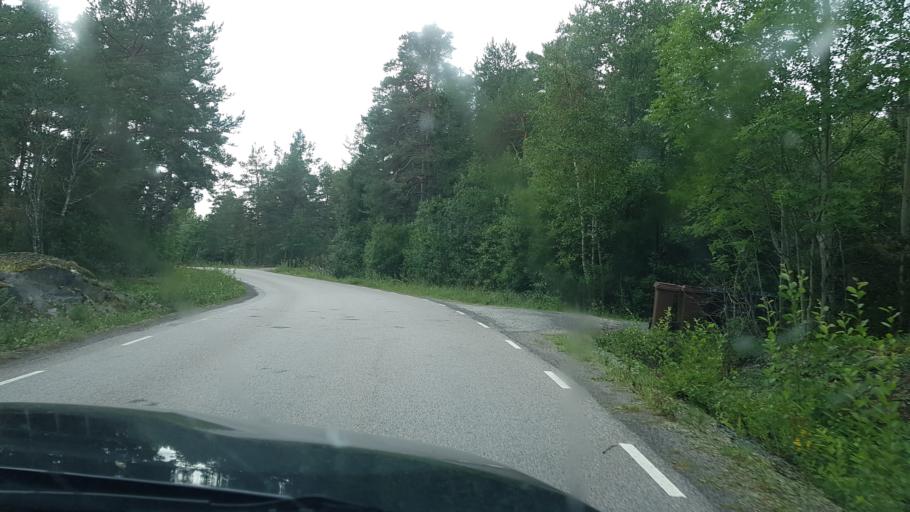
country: SE
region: Uppsala
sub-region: Osthammars Kommun
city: Oregrund
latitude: 60.3950
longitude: 18.4028
